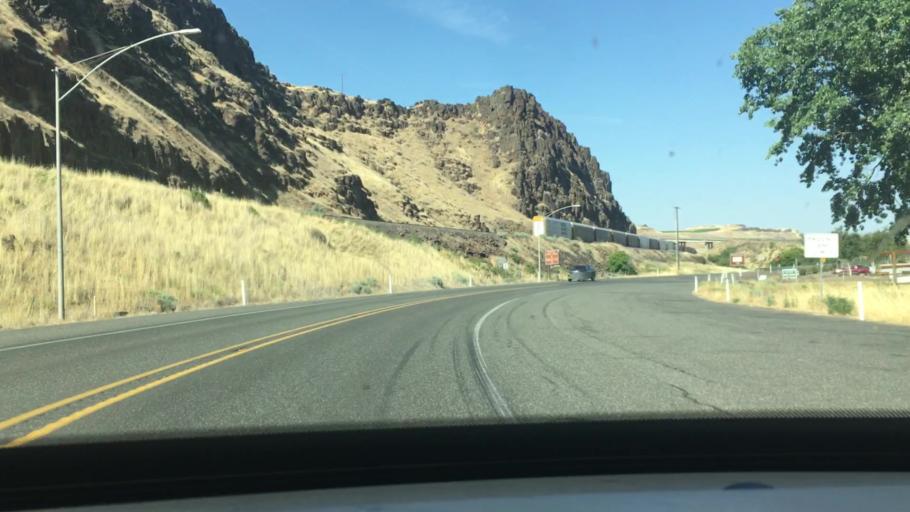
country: US
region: Washington
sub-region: Klickitat County
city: Goldendale
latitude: 45.6822
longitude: -120.8361
